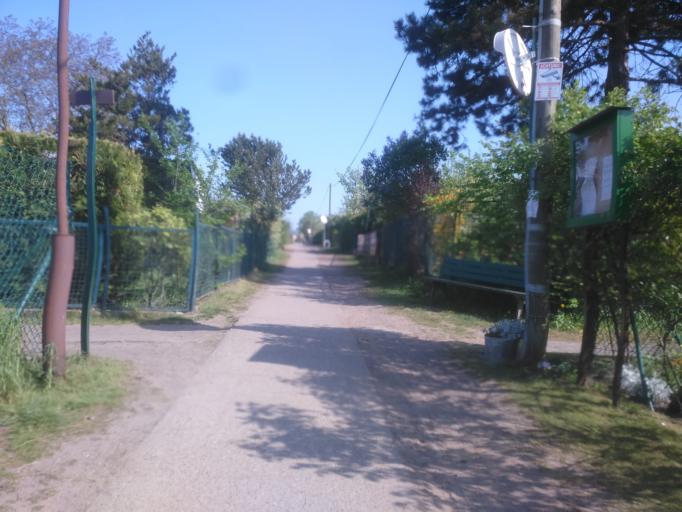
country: DE
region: Berlin
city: Fennpfuhl
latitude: 52.5384
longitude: 13.4632
